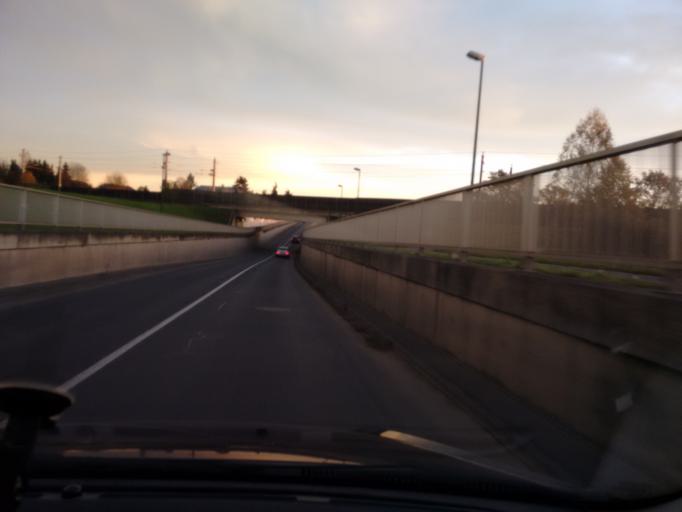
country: AT
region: Upper Austria
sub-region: Wels Stadt
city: Wels
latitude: 48.1767
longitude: 14.0063
